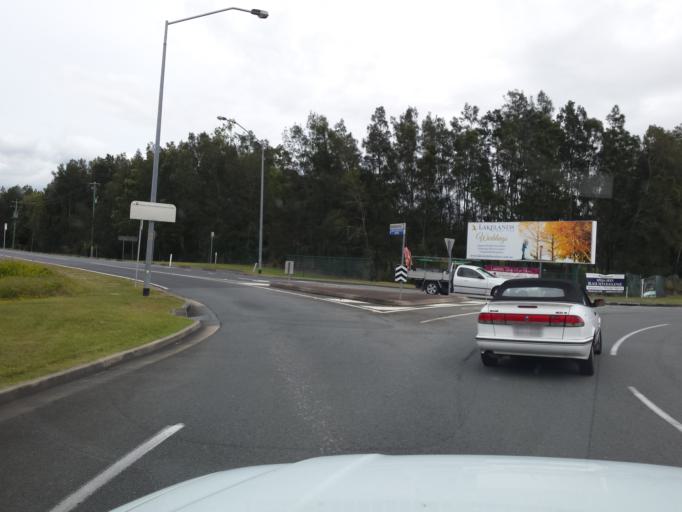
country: AU
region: Queensland
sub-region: Gold Coast
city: Clear Island Waters
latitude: -28.0442
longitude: 153.3885
